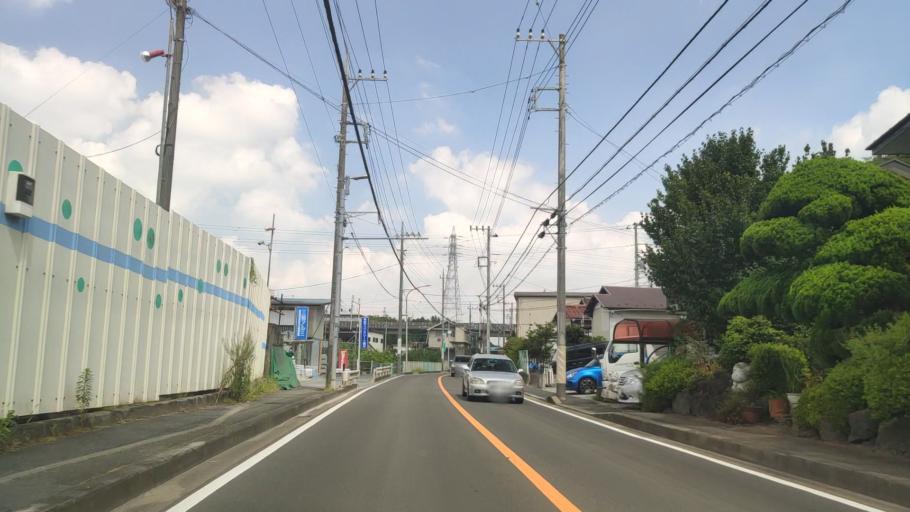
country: JP
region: Kanagawa
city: Minami-rinkan
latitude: 35.4446
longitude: 139.5056
